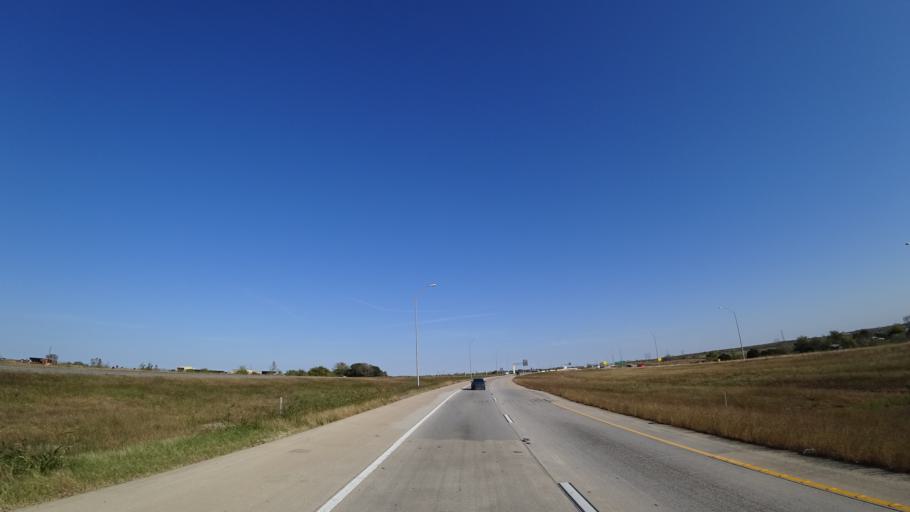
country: US
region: Texas
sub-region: Travis County
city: Manor
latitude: 30.3489
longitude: -97.5941
